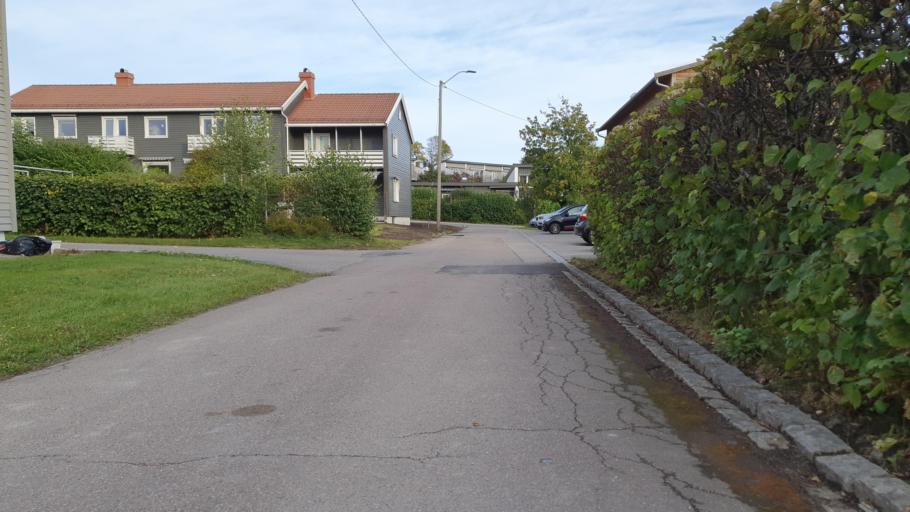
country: NO
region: Vestfold
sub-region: Tonsberg
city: Tonsberg
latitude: 59.2761
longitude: 10.4225
